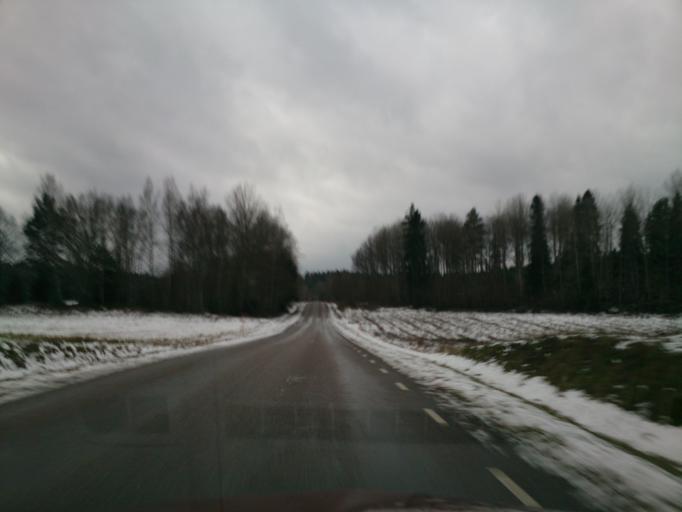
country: SE
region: OEstergoetland
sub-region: Atvidabergs Kommun
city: Atvidaberg
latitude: 58.2787
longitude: 16.0343
